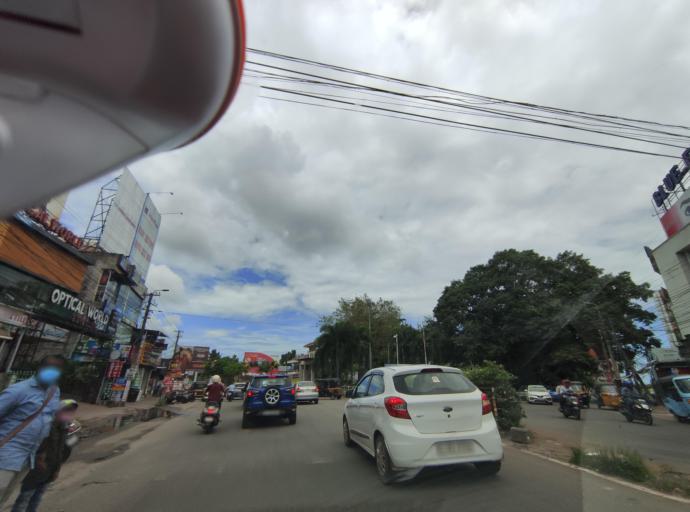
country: IN
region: Kerala
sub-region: Thiruvananthapuram
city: Thiruvananthapuram
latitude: 8.5299
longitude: 76.9387
